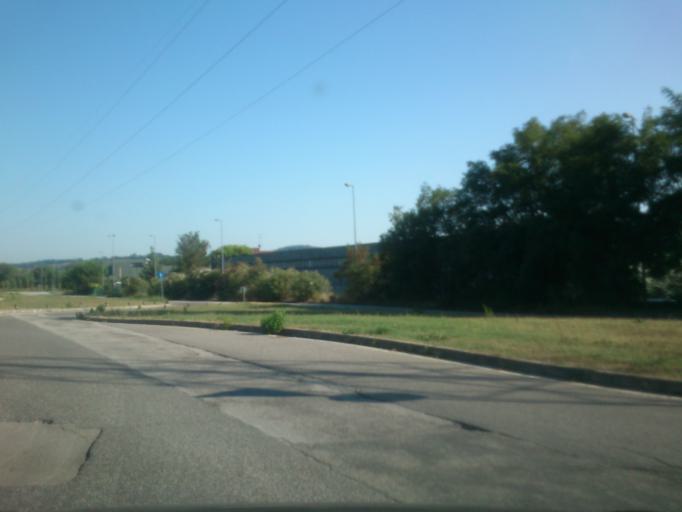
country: IT
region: The Marches
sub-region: Provincia di Pesaro e Urbino
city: Pesaro
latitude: 43.9019
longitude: 12.8573
